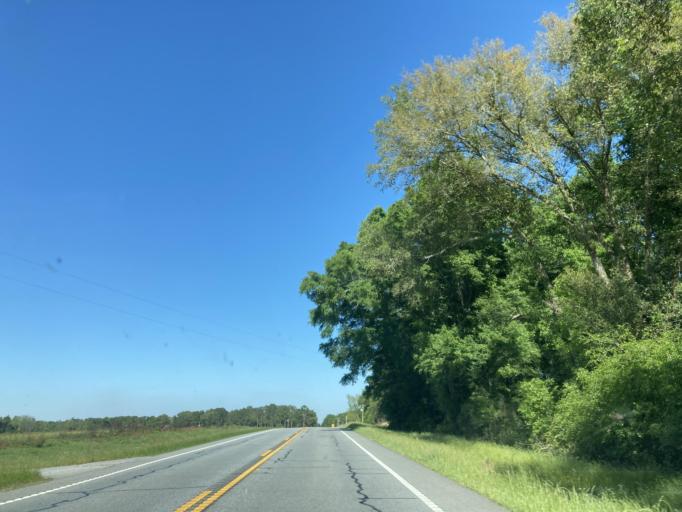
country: US
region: Georgia
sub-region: Baker County
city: Newton
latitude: 31.2695
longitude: -84.3930
